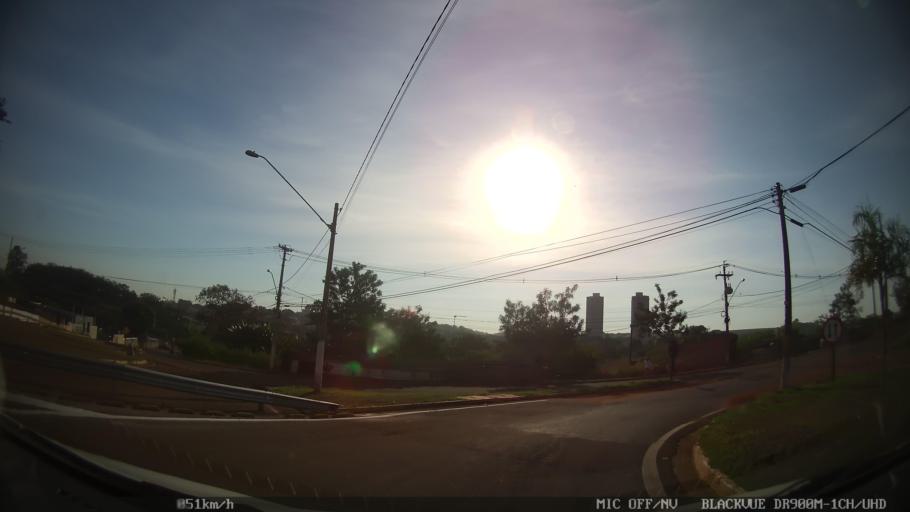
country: BR
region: Sao Paulo
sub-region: Ribeirao Preto
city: Ribeirao Preto
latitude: -21.2710
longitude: -47.8176
